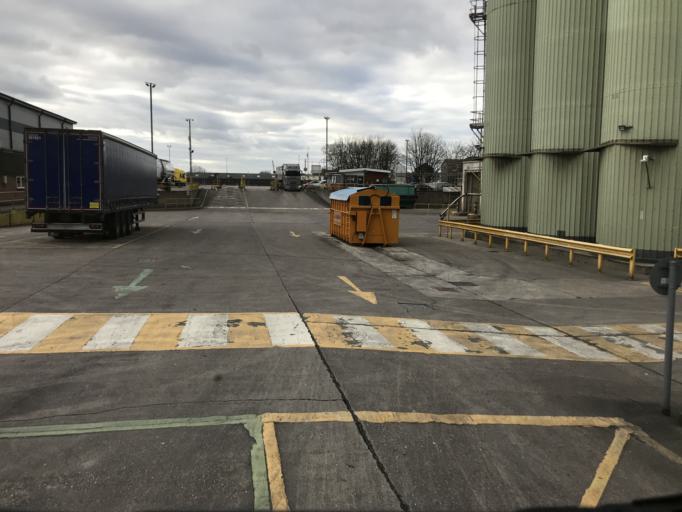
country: GB
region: England
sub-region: Trafford
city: Trafford Park
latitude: 53.4688
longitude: -2.3008
